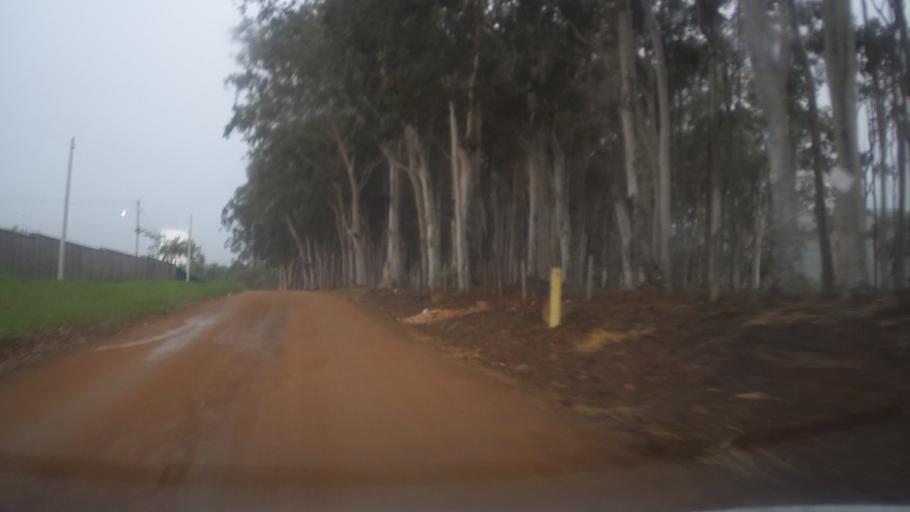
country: BR
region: Sao Paulo
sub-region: Jundiai
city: Jundiai
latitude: -23.2038
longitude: -46.9745
